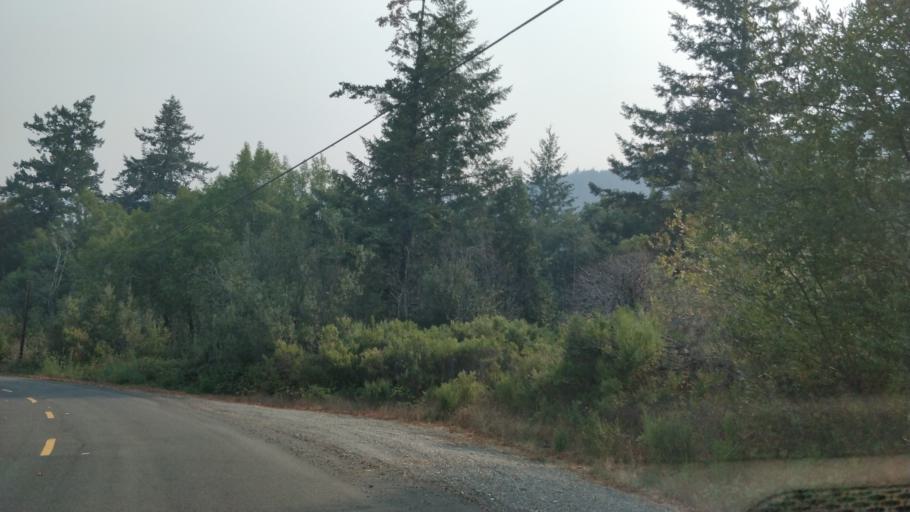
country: US
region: California
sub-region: Humboldt County
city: Rio Dell
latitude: 40.2858
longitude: -124.2526
